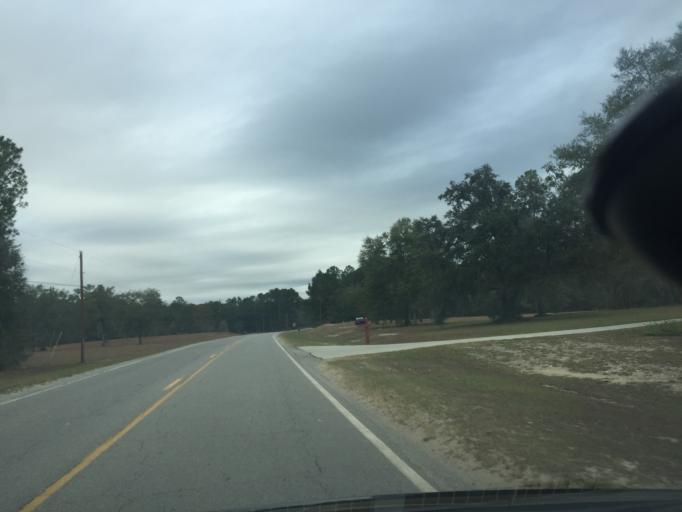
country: US
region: Georgia
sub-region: Chatham County
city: Bloomingdale
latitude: 32.1030
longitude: -81.3828
